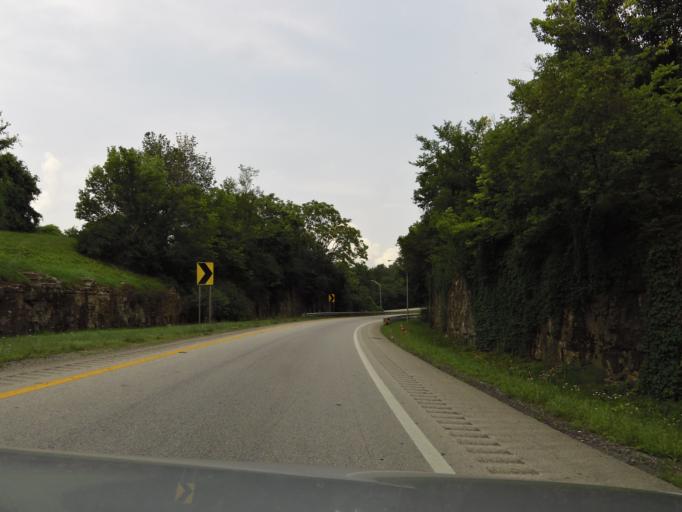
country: US
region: Kentucky
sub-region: Jefferson County
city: Northfield
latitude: 38.2876
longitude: -85.6441
